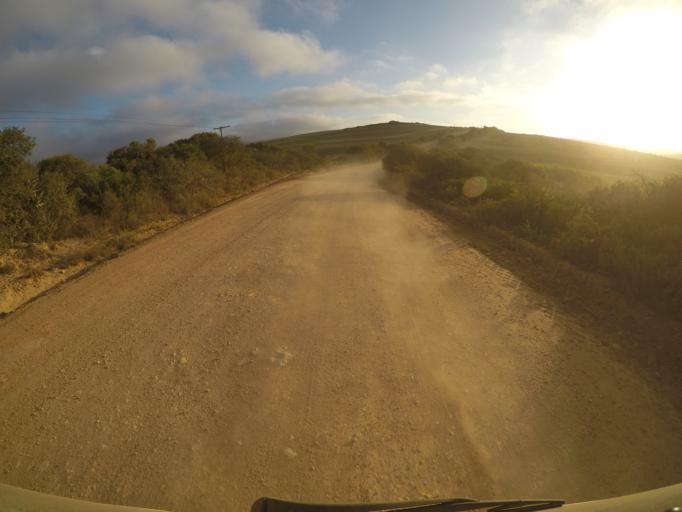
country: ZA
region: Western Cape
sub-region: Eden District Municipality
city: Mossel Bay
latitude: -34.1096
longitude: 22.0607
